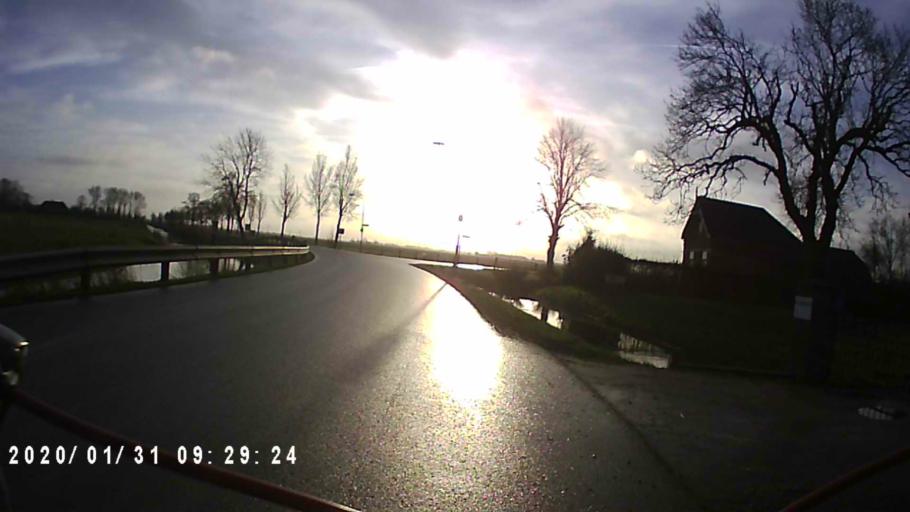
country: NL
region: Groningen
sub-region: Gemeente Zuidhorn
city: Aduard
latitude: 53.3047
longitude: 6.4482
